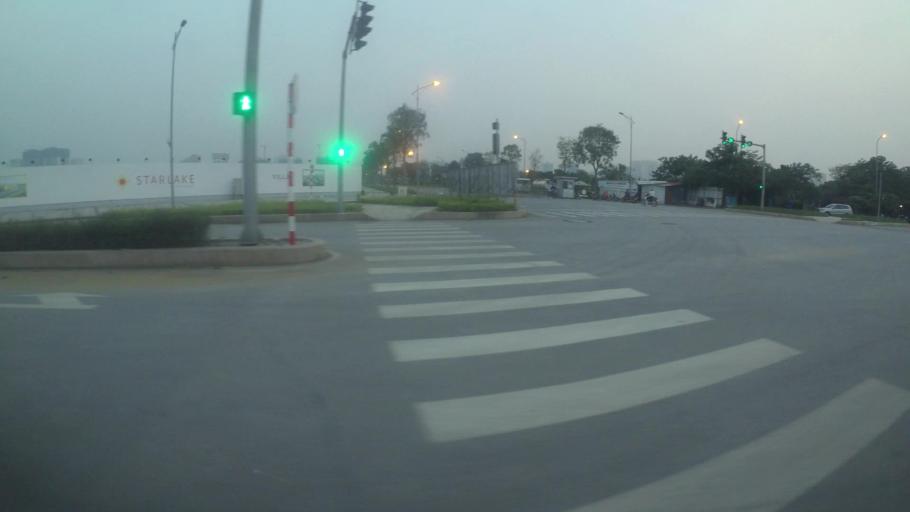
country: VN
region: Ha Noi
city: Tay Ho
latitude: 21.0625
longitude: 105.7902
